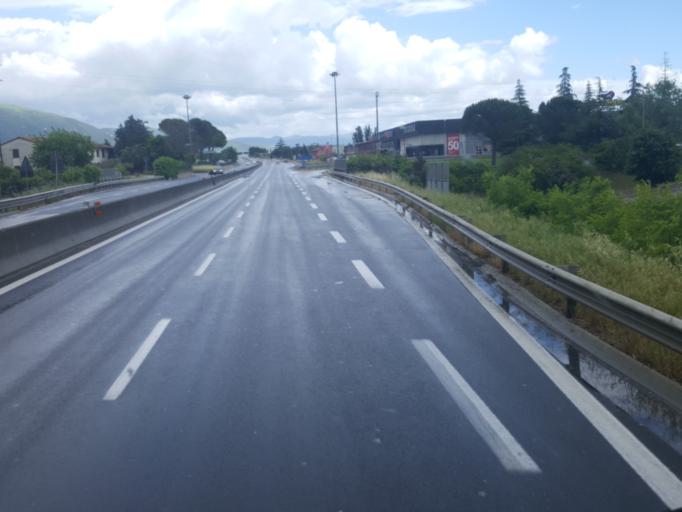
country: IT
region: Umbria
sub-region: Provincia di Perugia
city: Bastia umbra
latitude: 43.0626
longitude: 12.5454
